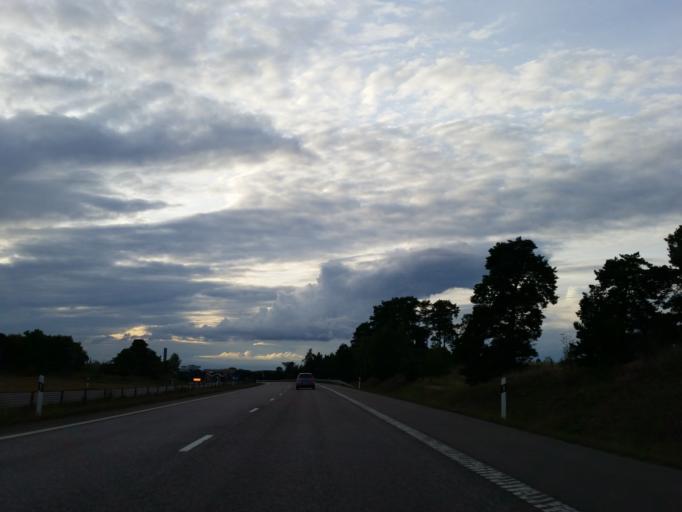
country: SE
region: Uppsala
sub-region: Uppsala Kommun
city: Saevja
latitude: 59.8400
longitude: 17.7230
